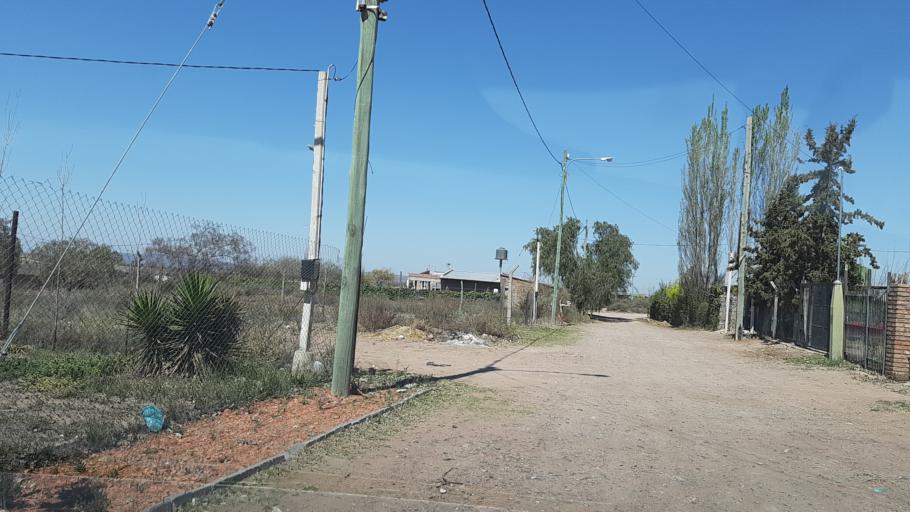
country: AR
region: Mendoza
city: Lujan de Cuyo
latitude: -33.0171
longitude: -68.9513
